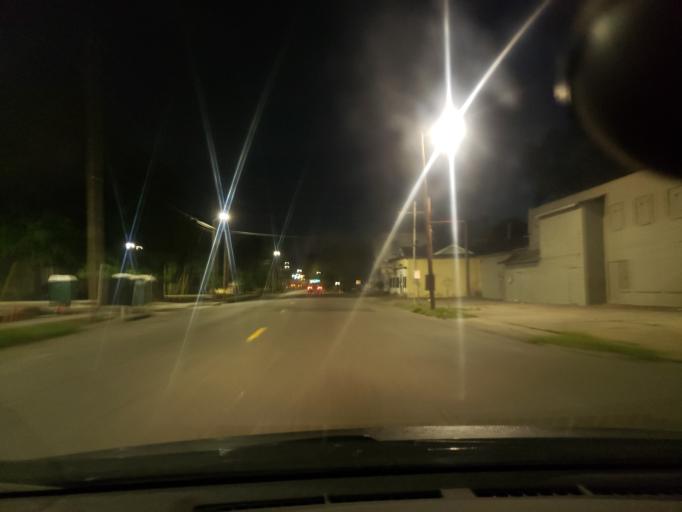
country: US
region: Georgia
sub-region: Chatham County
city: Savannah
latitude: 32.0607
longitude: -81.1035
